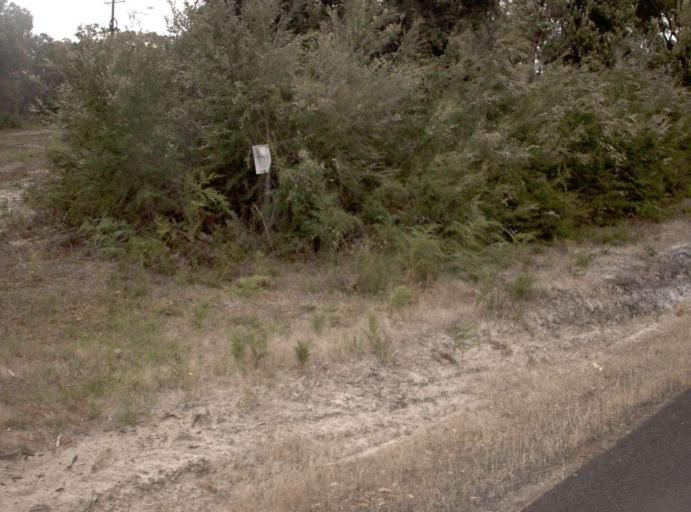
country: AU
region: Victoria
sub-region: Wellington
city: Sale
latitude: -38.3426
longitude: 147.0044
